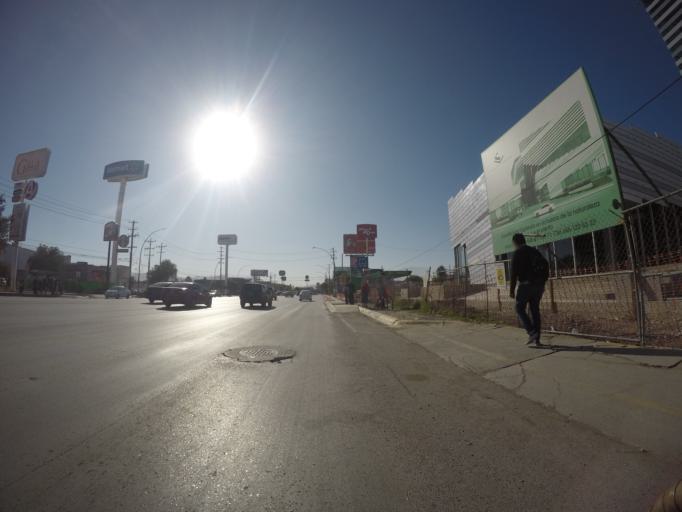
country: MX
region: Chihuahua
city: Ciudad Juarez
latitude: 31.7374
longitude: -106.4429
